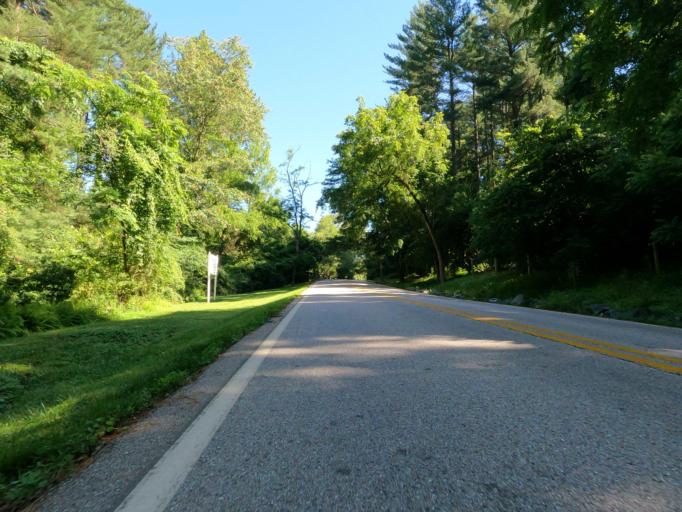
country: US
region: Maryland
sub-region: Howard County
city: Riverside
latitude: 39.2025
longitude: -76.9186
